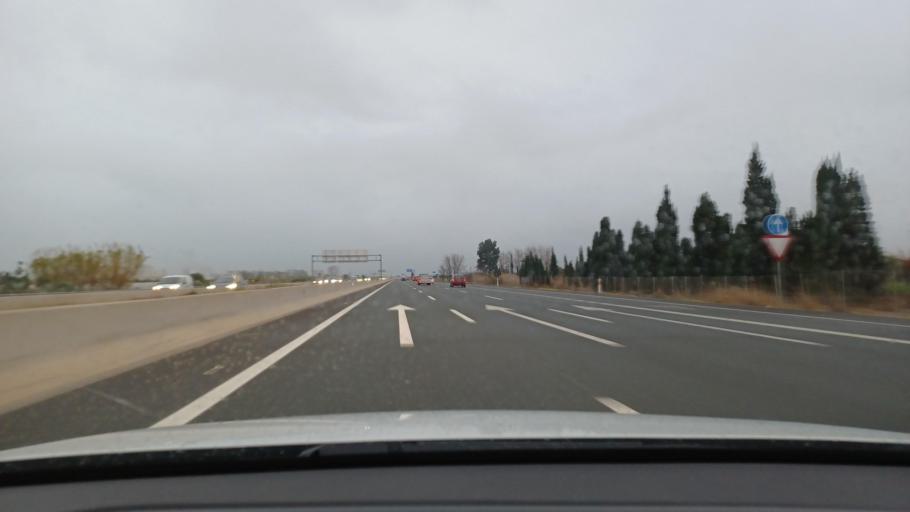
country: ES
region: Valencia
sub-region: Provincia de Valencia
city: Puig
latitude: 39.5850
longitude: -0.2940
